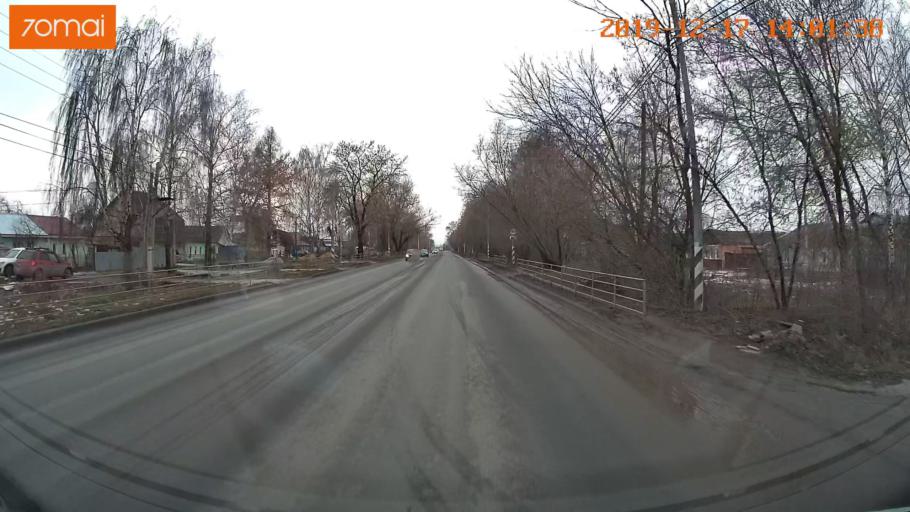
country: RU
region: Rjazan
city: Ryazan'
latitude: 54.6188
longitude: 39.6556
